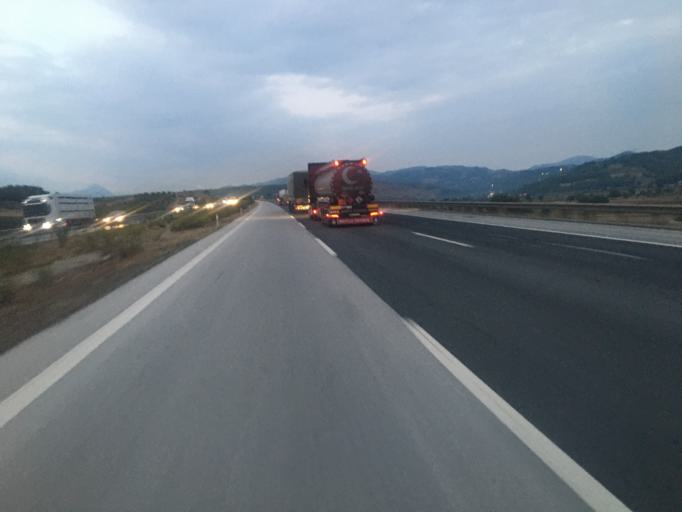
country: TR
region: Osmaniye
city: Kaypak
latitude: 37.1543
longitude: 36.3498
